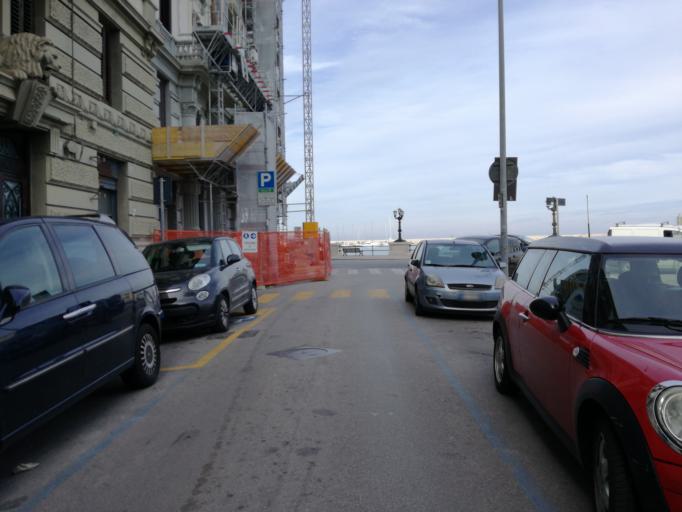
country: IT
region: Apulia
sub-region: Provincia di Bari
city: Bari
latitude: 41.1230
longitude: 16.8771
